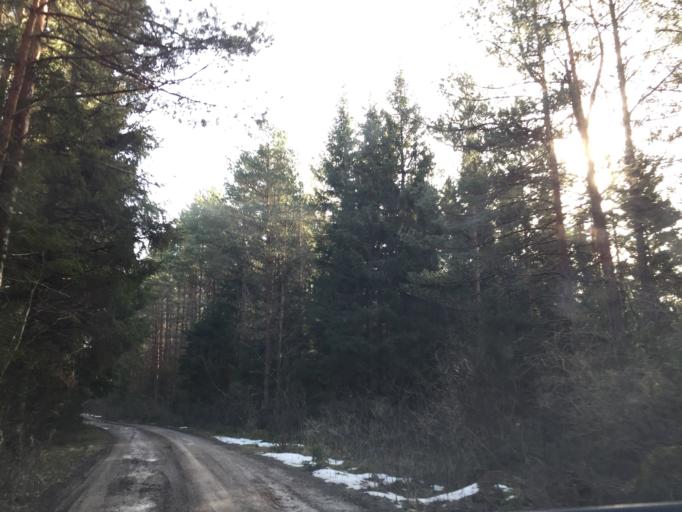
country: EE
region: Saare
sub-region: Kuressaare linn
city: Kuressaare
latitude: 58.3773
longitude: 22.0097
